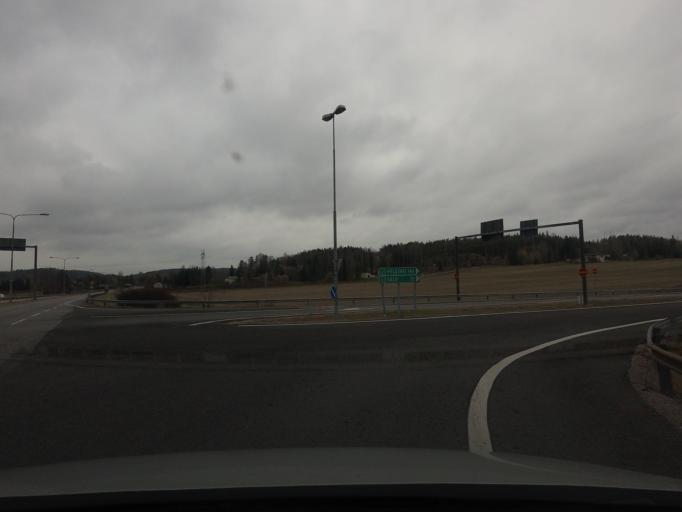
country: FI
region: Varsinais-Suomi
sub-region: Turku
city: Piikkioe
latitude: 60.4412
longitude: 22.6007
